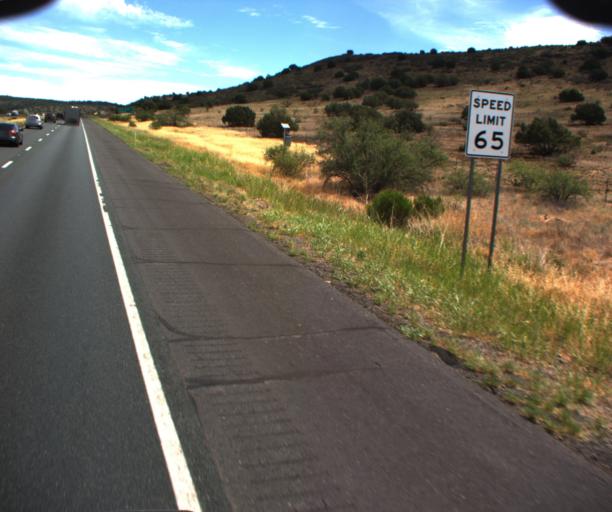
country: US
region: Arizona
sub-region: Yavapai County
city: Camp Verde
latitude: 34.5240
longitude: -111.9849
